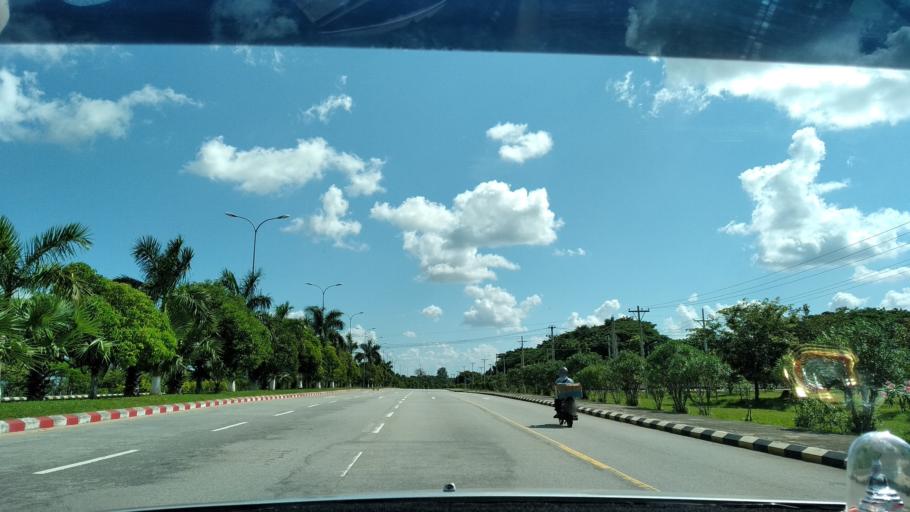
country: MM
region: Mandalay
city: Nay Pyi Taw
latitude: 19.7857
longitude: 96.1445
